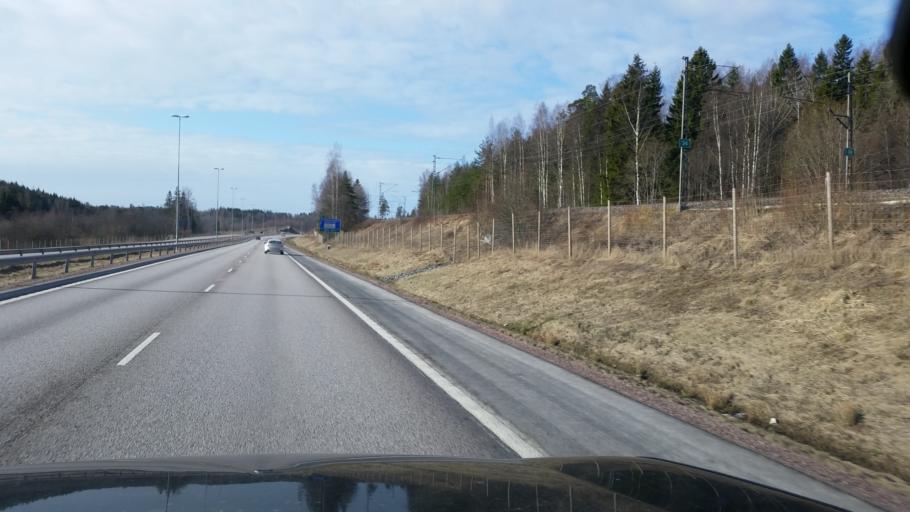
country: FI
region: Uusimaa
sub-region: Helsinki
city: Kirkkonummi
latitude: 60.1279
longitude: 24.4923
